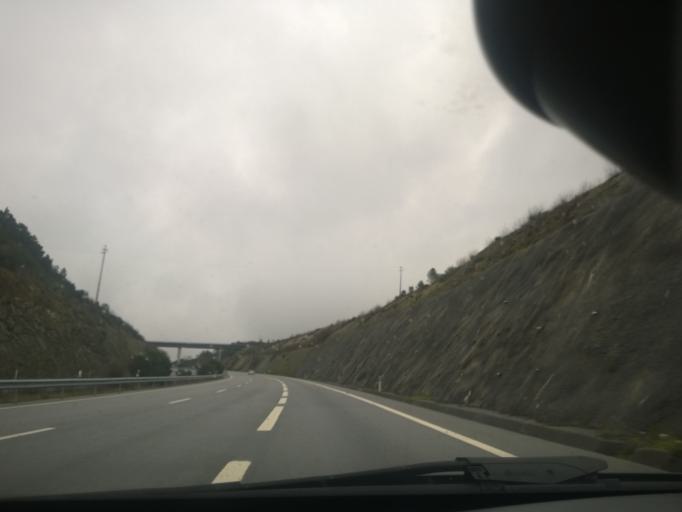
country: PT
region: Braga
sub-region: Celorico de Basto
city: Celorico de Basto
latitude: 41.4483
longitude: -8.0665
